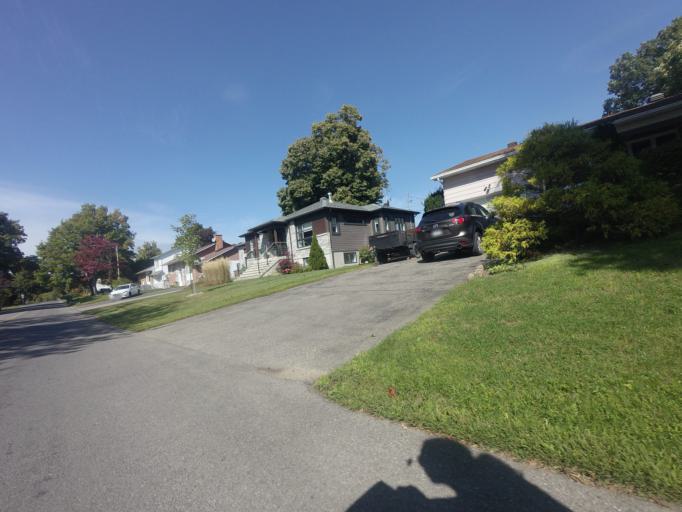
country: CA
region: Quebec
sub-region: Laurentides
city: Saint-Eustache
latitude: 45.5551
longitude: -73.9068
